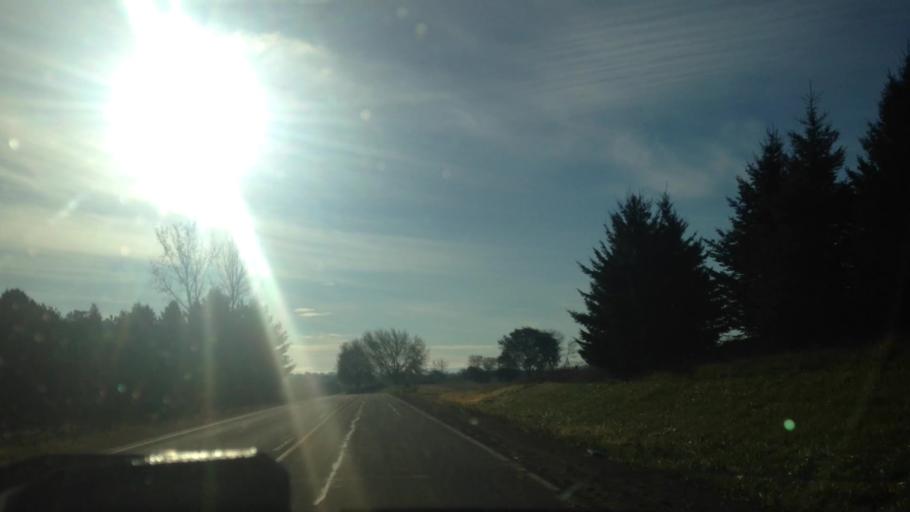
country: US
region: Wisconsin
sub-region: Dodge County
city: Mayville
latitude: 43.4808
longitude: -88.5072
